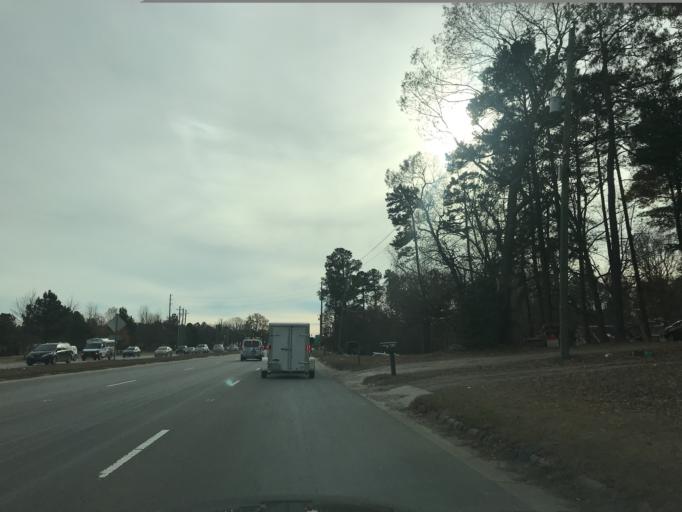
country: US
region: North Carolina
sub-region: Wake County
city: Knightdale
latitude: 35.8672
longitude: -78.5460
